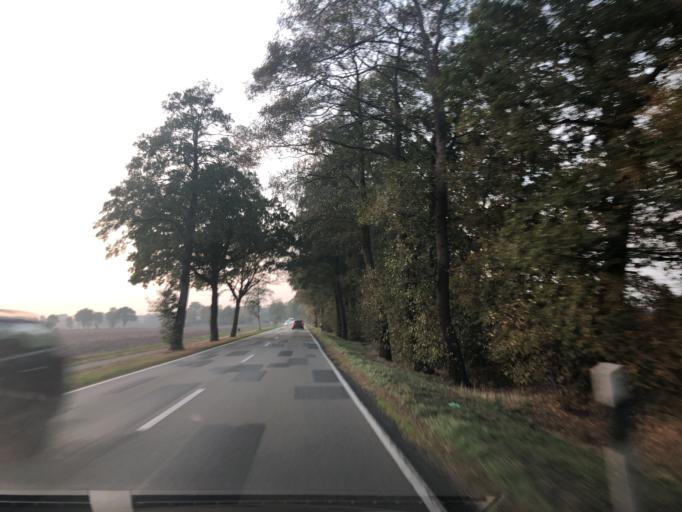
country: DE
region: Lower Saxony
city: Bosel
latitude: 52.9995
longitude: 7.9930
